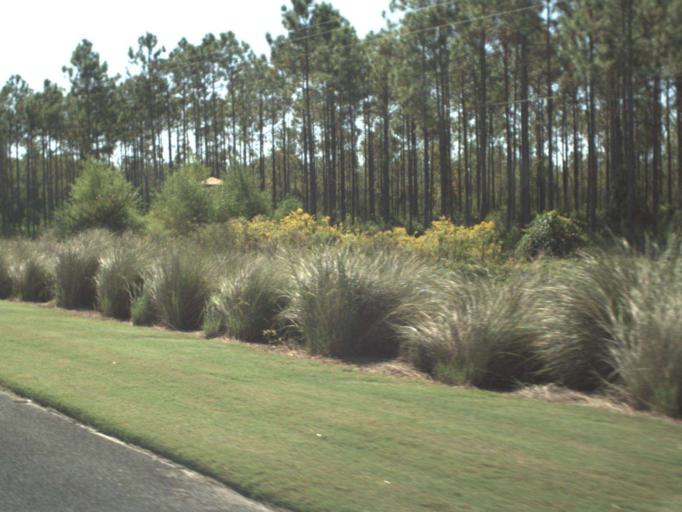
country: US
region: Florida
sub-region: Bay County
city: Laguna Beach
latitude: 30.2948
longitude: -86.0237
